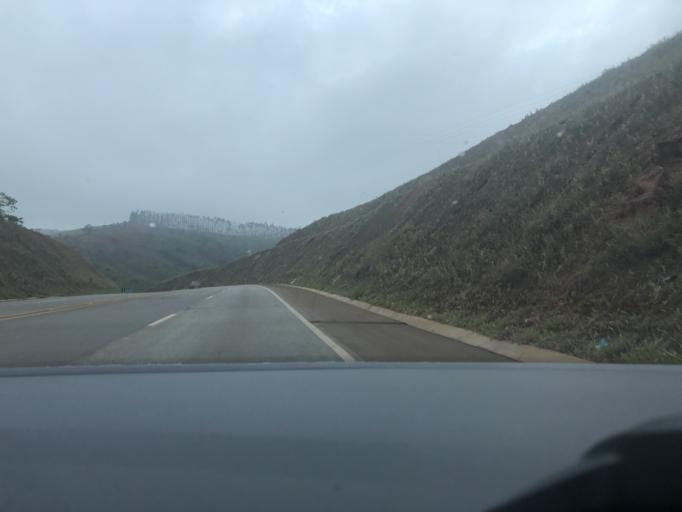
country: BR
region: Minas Gerais
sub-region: Congonhas
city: Congonhas
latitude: -20.6105
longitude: -43.9304
